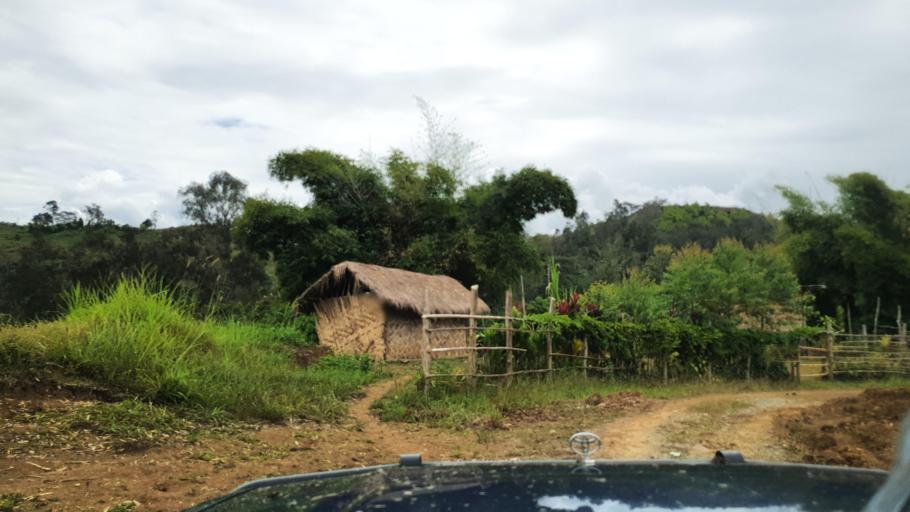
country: PG
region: Jiwaka
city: Minj
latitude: -5.9288
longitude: 144.7442
